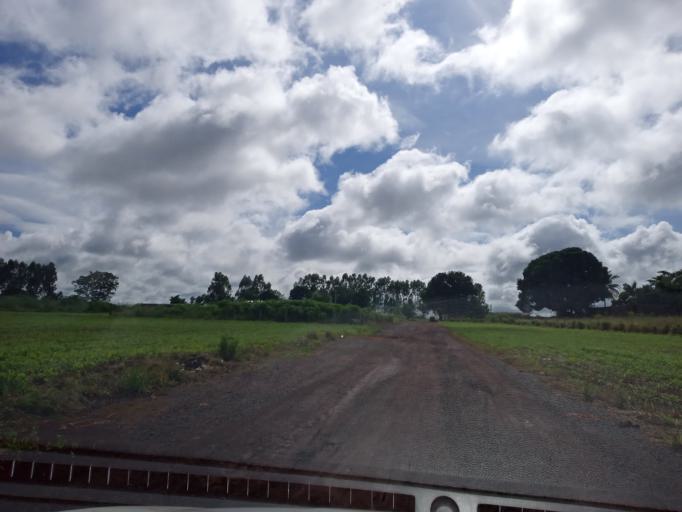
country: BR
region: Minas Gerais
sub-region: Centralina
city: Centralina
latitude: -18.5790
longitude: -49.1954
